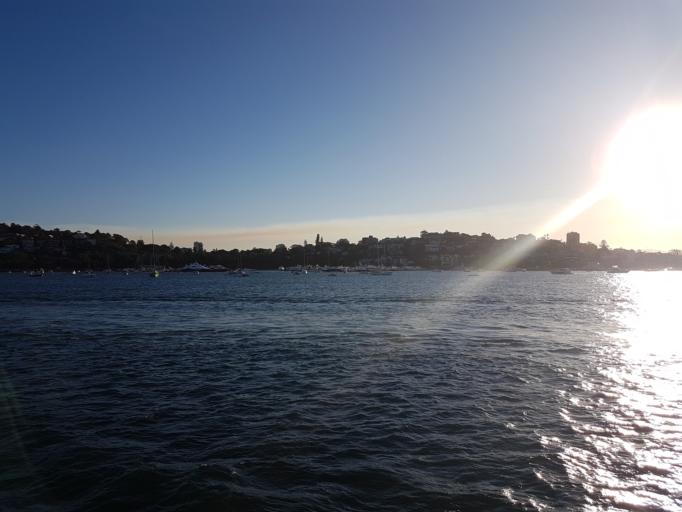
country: AU
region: New South Wales
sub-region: Woollahra
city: Point Piper
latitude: -33.8672
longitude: 151.2624
